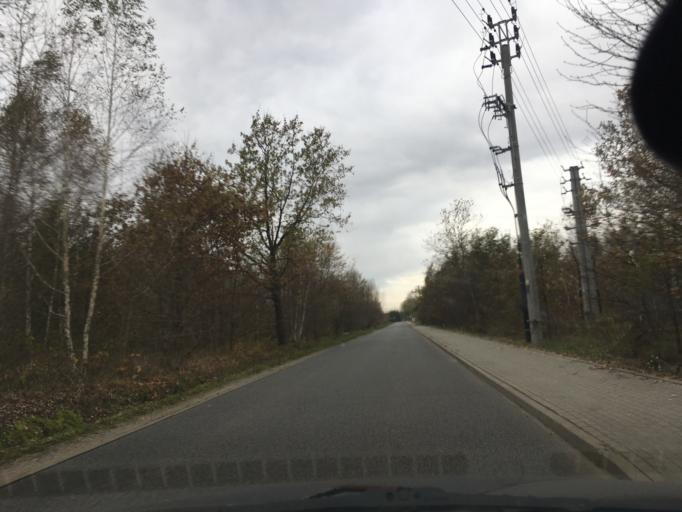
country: PL
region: Lodz Voivodeship
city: Zabia Wola
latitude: 52.0237
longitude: 20.7114
